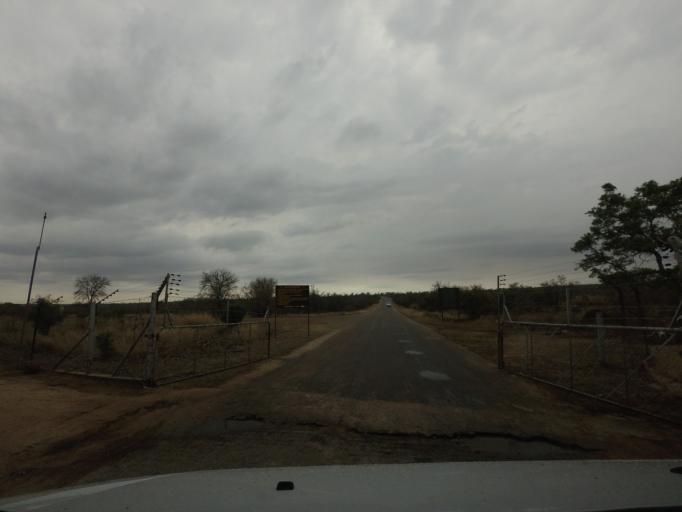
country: ZA
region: Limpopo
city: Thulamahashi
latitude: -24.4758
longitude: 31.3910
